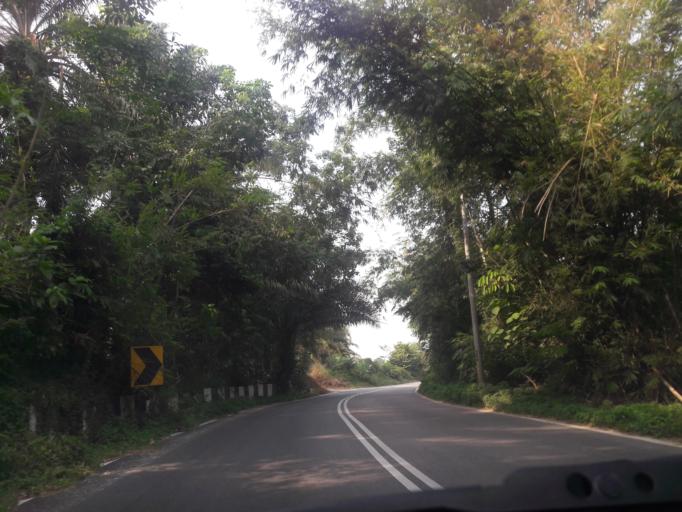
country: MY
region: Kedah
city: Kulim
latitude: 5.3646
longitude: 100.5228
